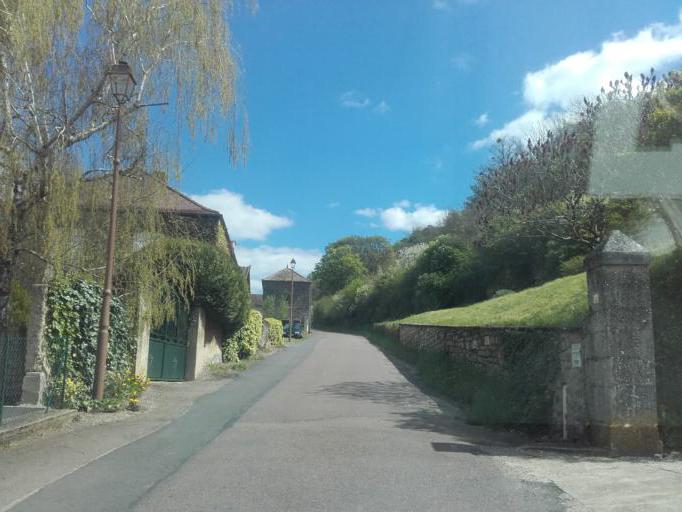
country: FR
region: Bourgogne
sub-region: Departement de la Cote-d'Or
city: Meursault
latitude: 46.9999
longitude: 4.7099
